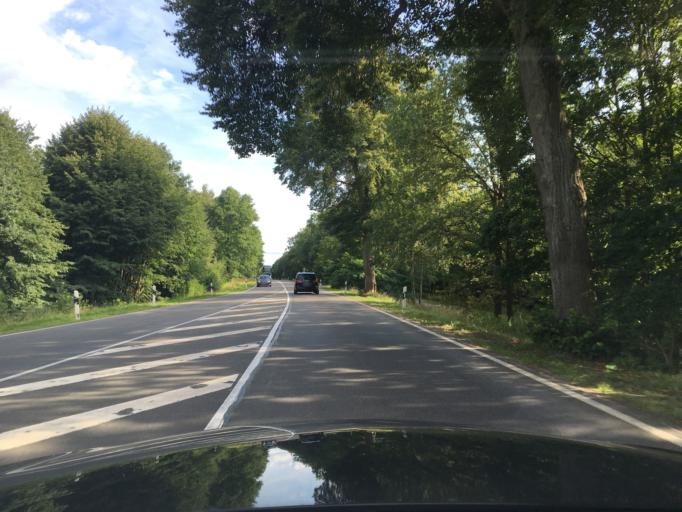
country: DE
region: Mecklenburg-Vorpommern
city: Neustrelitz
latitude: 53.3943
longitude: 13.0441
